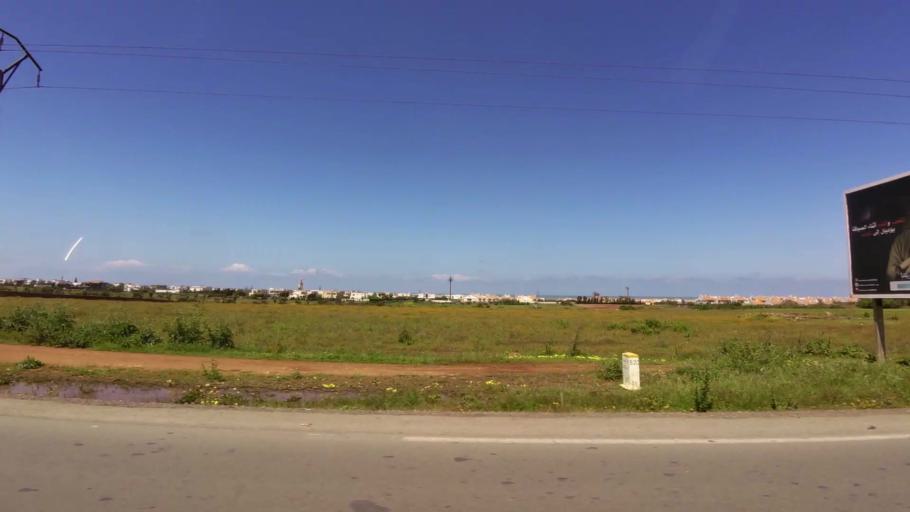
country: MA
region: Grand Casablanca
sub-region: Nouaceur
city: Dar Bouazza
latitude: 33.5297
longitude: -7.7744
